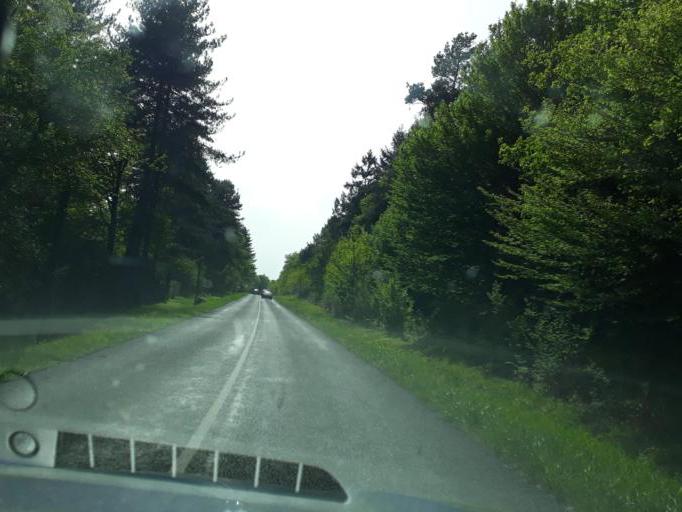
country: FR
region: Centre
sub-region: Departement du Loir-et-Cher
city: Dhuizon
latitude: 47.6594
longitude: 1.6611
